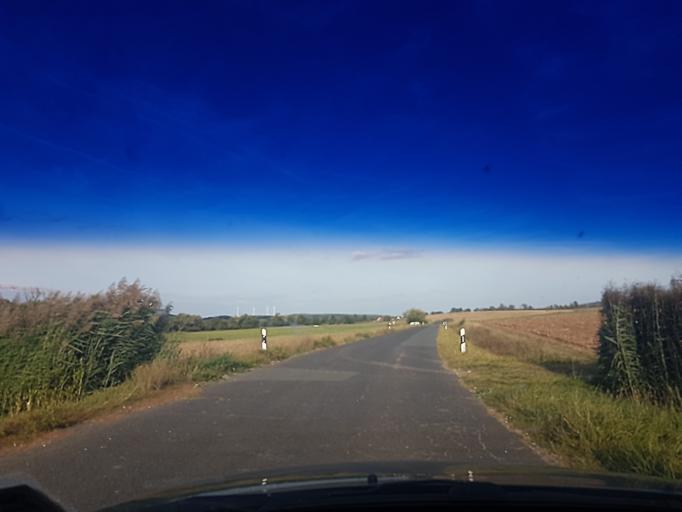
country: DE
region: Bavaria
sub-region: Regierungsbezirk Mittelfranken
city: Wachenroth
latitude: 49.7411
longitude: 10.6684
